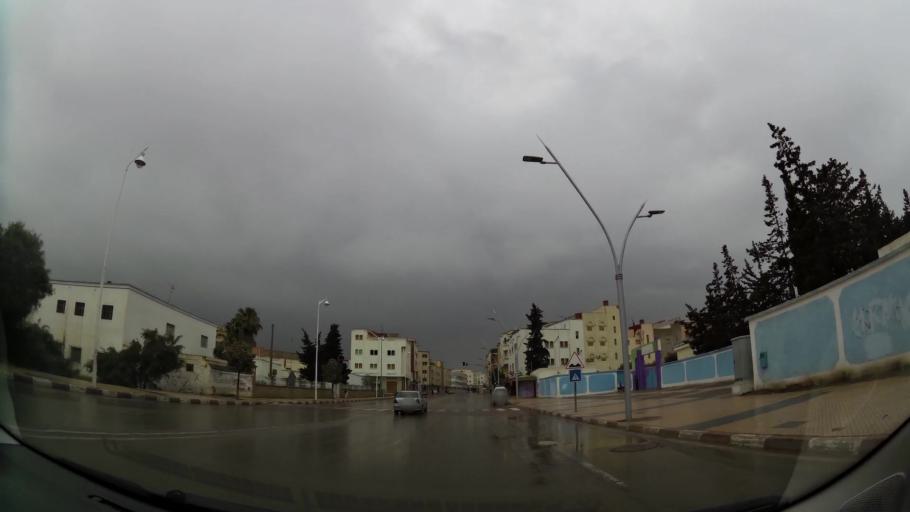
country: MA
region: Oriental
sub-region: Nador
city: Nador
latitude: 35.1540
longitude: -2.9858
